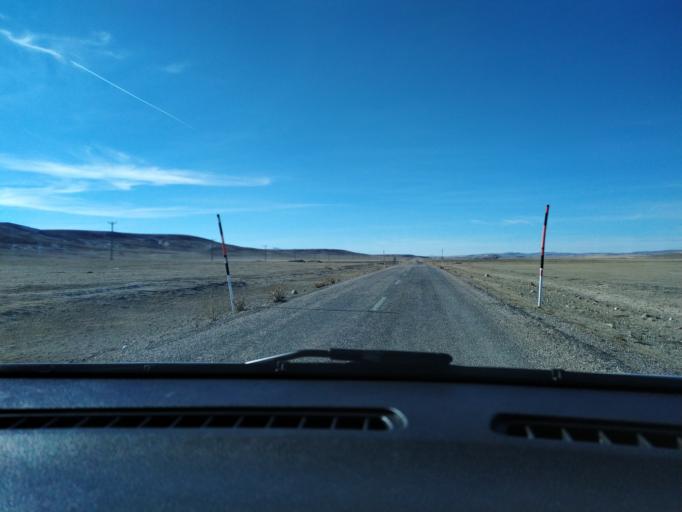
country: TR
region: Kayseri
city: Orensehir
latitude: 39.0974
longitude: 36.6954
